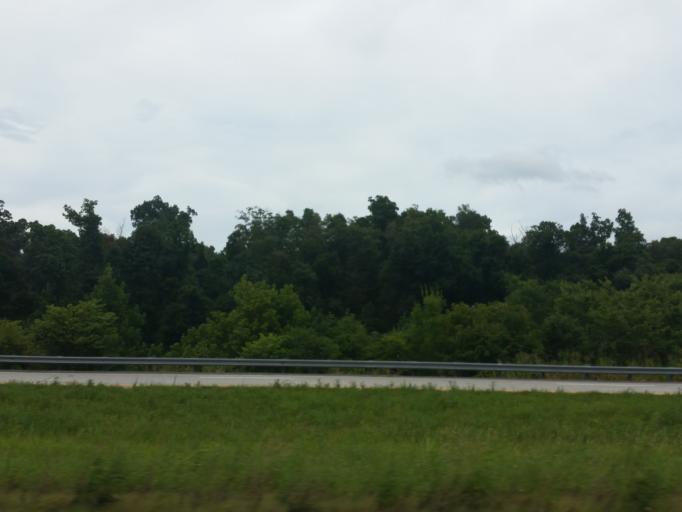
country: US
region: Kentucky
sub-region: Lyon County
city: Eddyville
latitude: 37.0251
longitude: -87.9933
